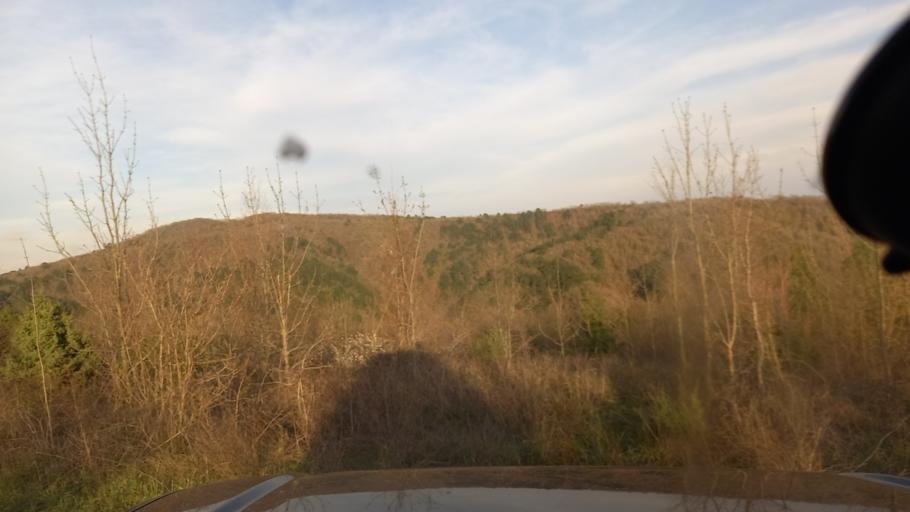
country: RU
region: Krasnodarskiy
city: Arkhipo-Osipovka
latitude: 44.3612
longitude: 38.5684
